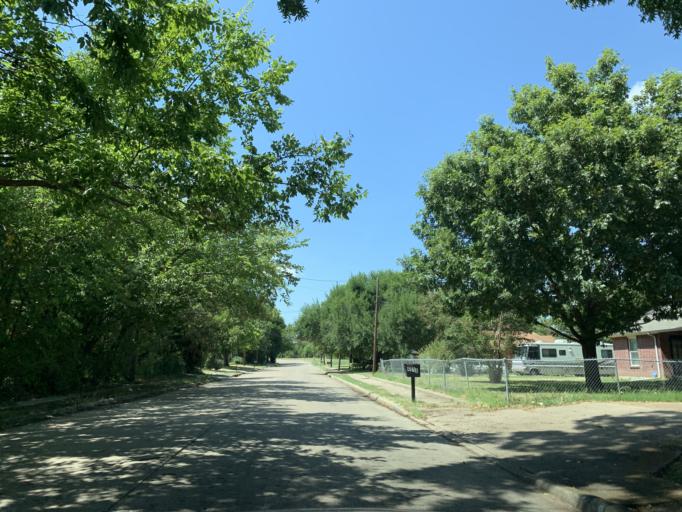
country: US
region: Texas
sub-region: Dallas County
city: Hutchins
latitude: 32.7045
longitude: -96.7658
